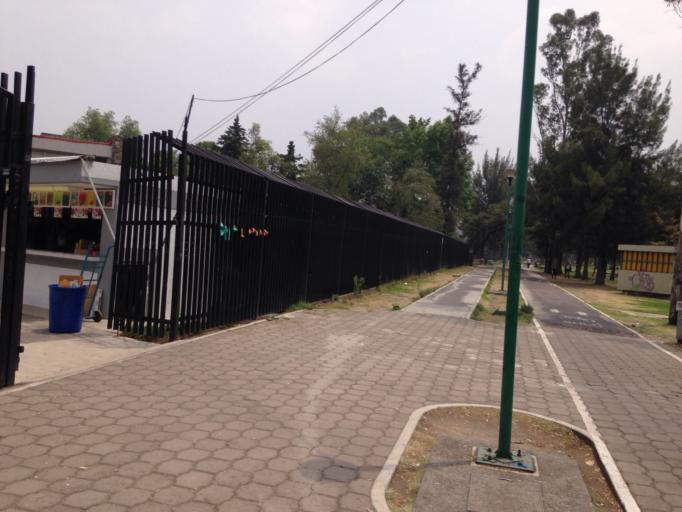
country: MX
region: Mexico City
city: Coyoacan
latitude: 19.3275
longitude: -99.1829
